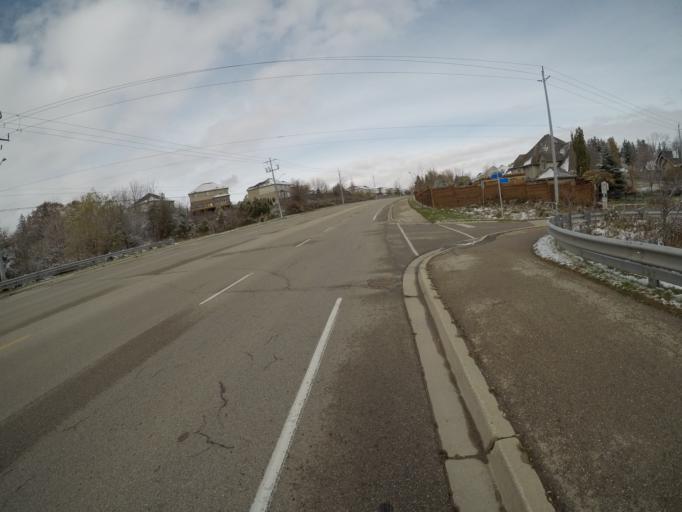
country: CA
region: Ontario
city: Waterloo
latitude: 43.5051
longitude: -80.4969
